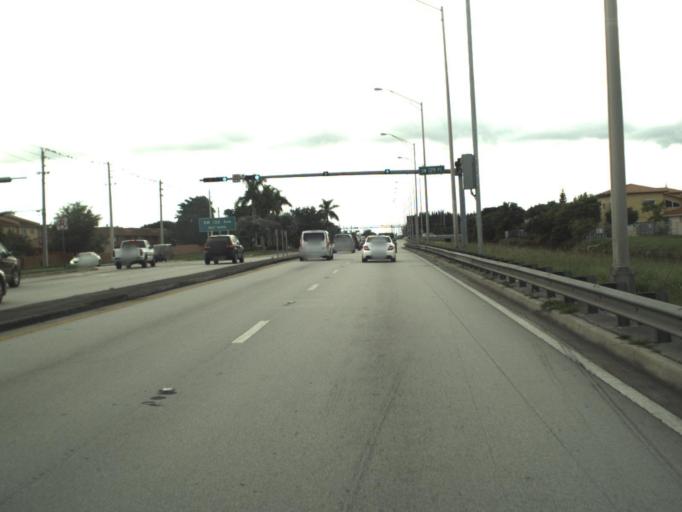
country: US
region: Florida
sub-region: Miami-Dade County
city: Tamiami
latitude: 25.7611
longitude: -80.4054
